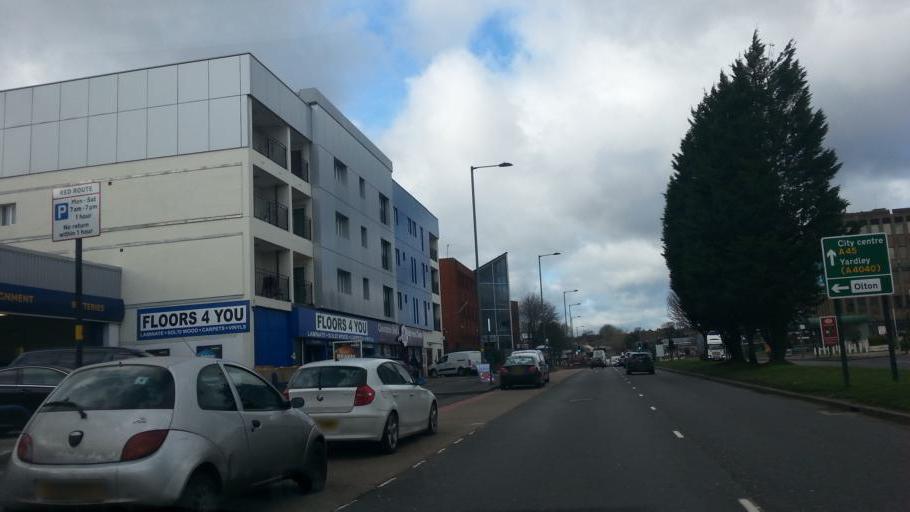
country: GB
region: England
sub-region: City and Borough of Birmingham
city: Acocks Green
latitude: 52.4528
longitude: -1.7868
